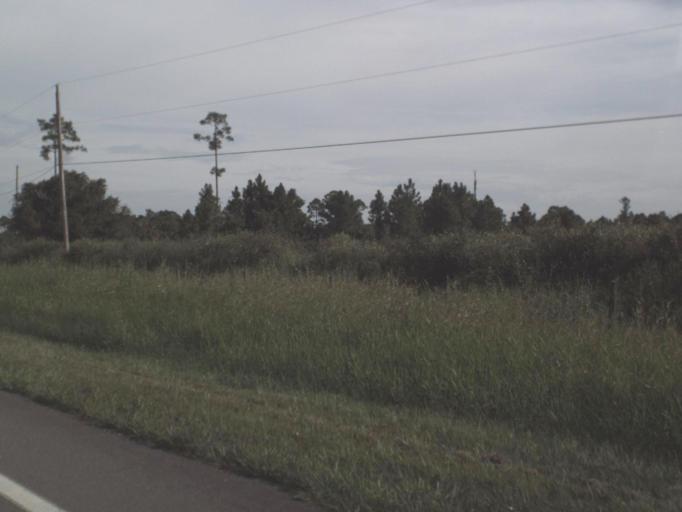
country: US
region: Florida
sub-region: Lee County
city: Olga
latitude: 26.8646
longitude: -81.7597
